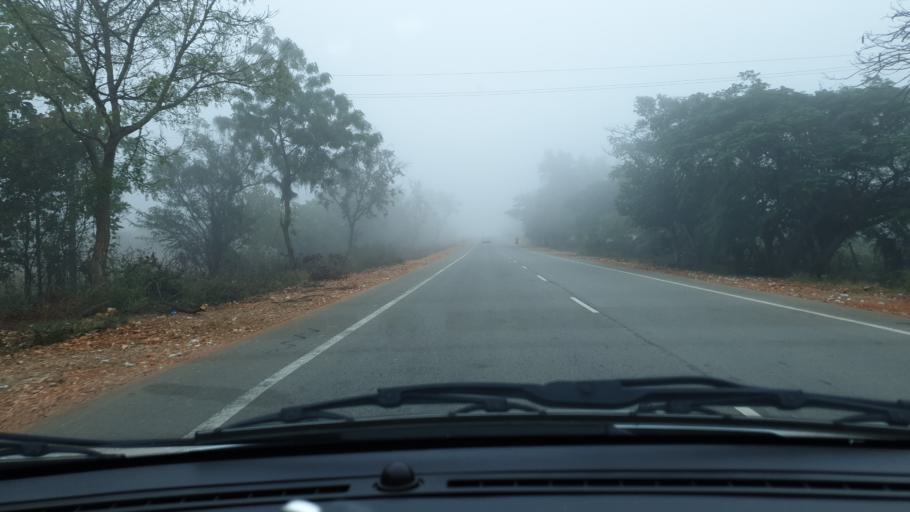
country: IN
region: Telangana
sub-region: Mahbubnagar
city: Nagar Karnul
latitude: 16.6397
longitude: 78.5945
